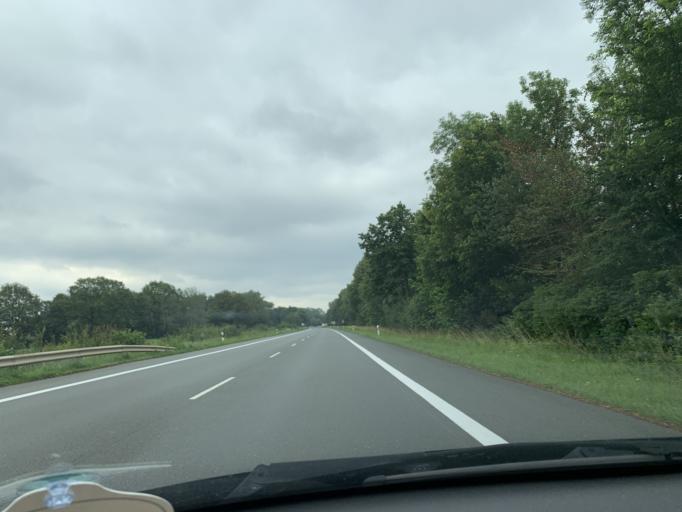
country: DE
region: North Rhine-Westphalia
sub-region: Regierungsbezirk Munster
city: Ennigerloh
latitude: 51.9063
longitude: 8.0498
